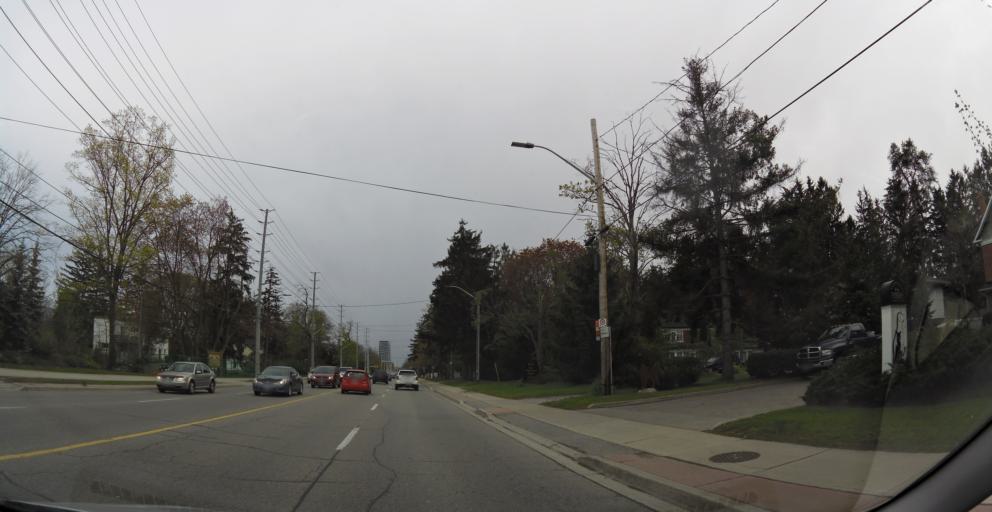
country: CA
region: Ontario
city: Mississauga
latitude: 43.5635
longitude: -79.5932
